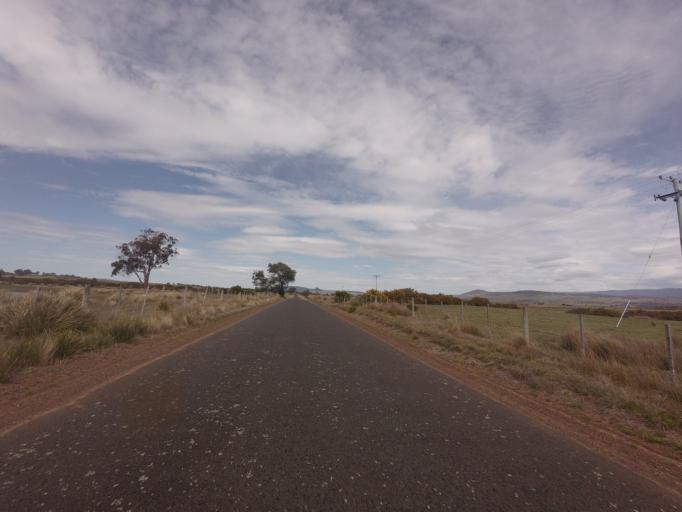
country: AU
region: Tasmania
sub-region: Northern Midlands
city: Evandale
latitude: -41.8367
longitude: 147.3307
